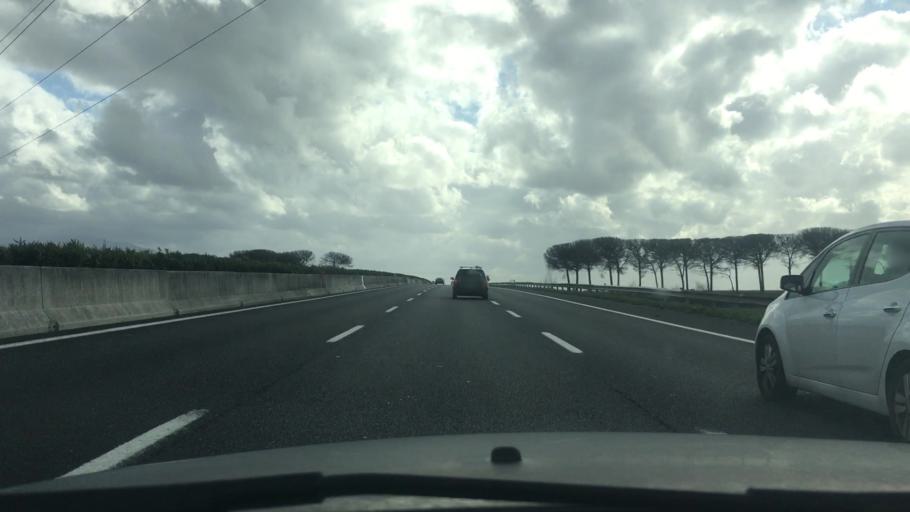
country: IT
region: Campania
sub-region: Provincia di Napoli
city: Pascarola
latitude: 40.9888
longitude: 14.3249
